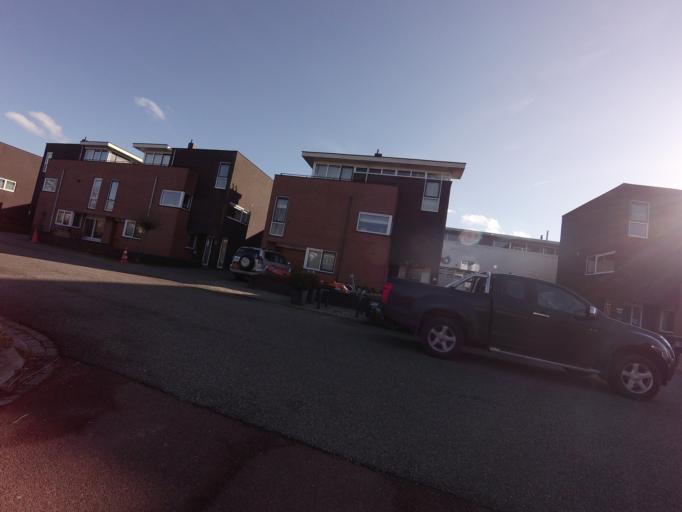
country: NL
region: Utrecht
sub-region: Gemeente IJsselstein
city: IJsselstein
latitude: 52.0082
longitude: 5.0476
